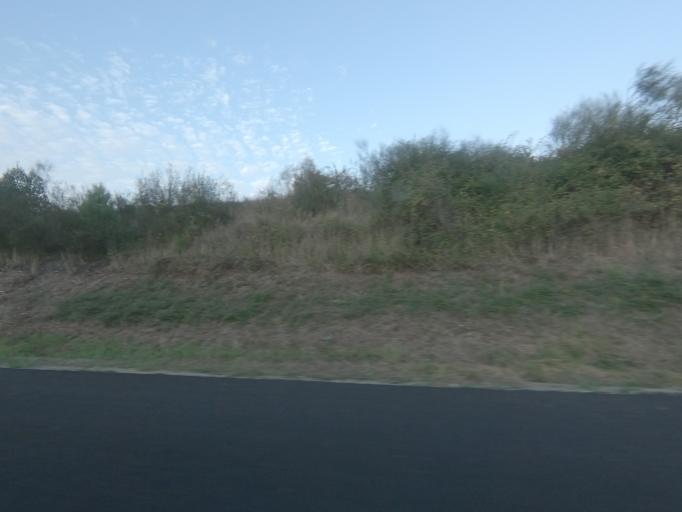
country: PT
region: Leiria
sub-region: Leiria
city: Caranguejeira
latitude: 39.8099
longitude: -8.7222
